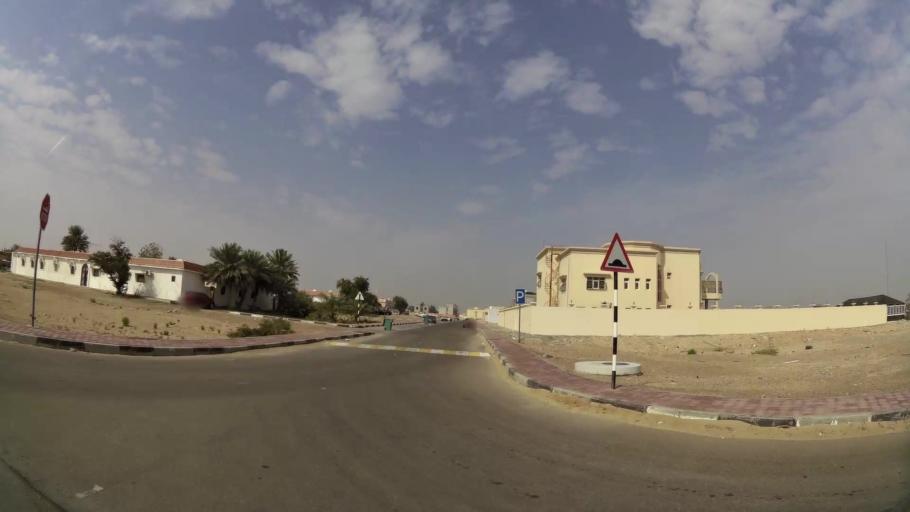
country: AE
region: Abu Dhabi
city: Abu Dhabi
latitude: 24.2746
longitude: 54.6715
